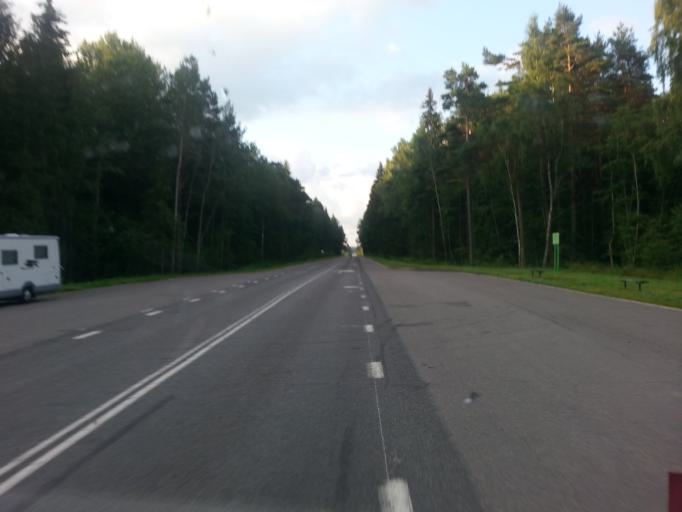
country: BY
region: Minsk
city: Kryvichy
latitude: 54.6193
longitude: 27.1722
